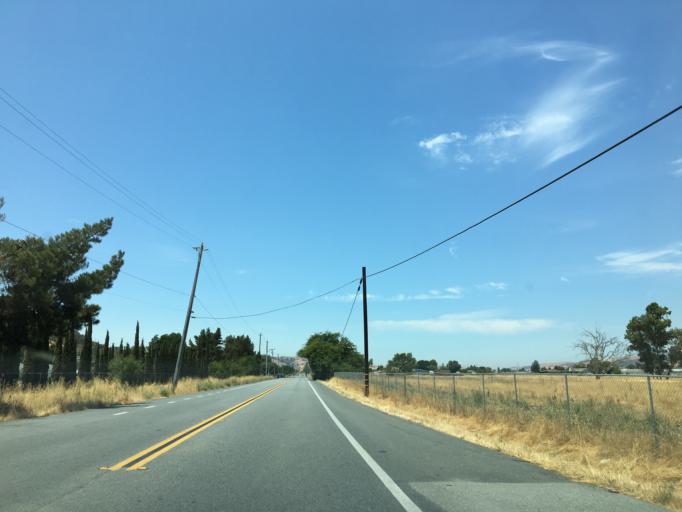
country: US
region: California
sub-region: Santa Clara County
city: Morgan Hill
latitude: 37.1578
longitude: -121.6930
